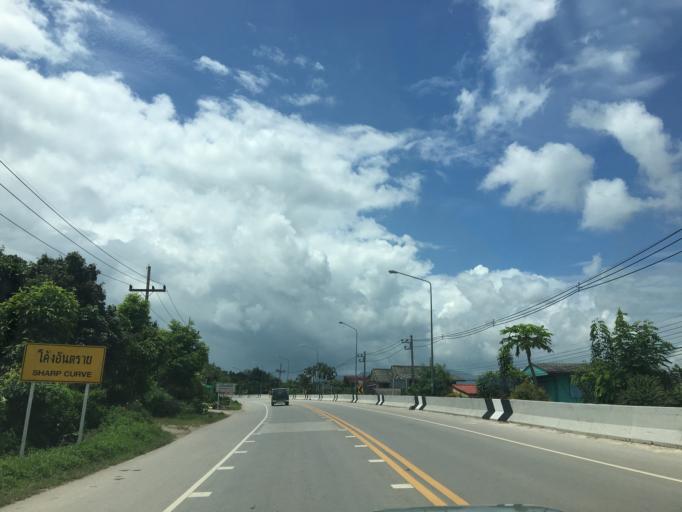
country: TH
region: Chiang Rai
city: Pa Daet
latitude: 19.6586
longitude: 99.9333
